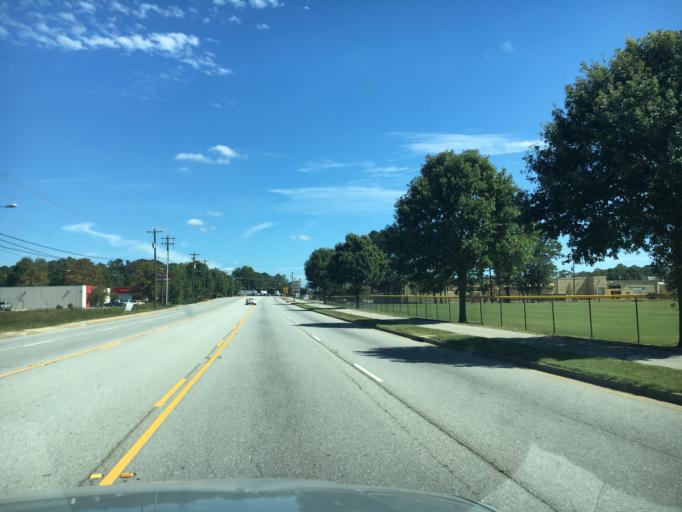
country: US
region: South Carolina
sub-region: Spartanburg County
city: Spartanburg
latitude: 34.9197
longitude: -81.8917
